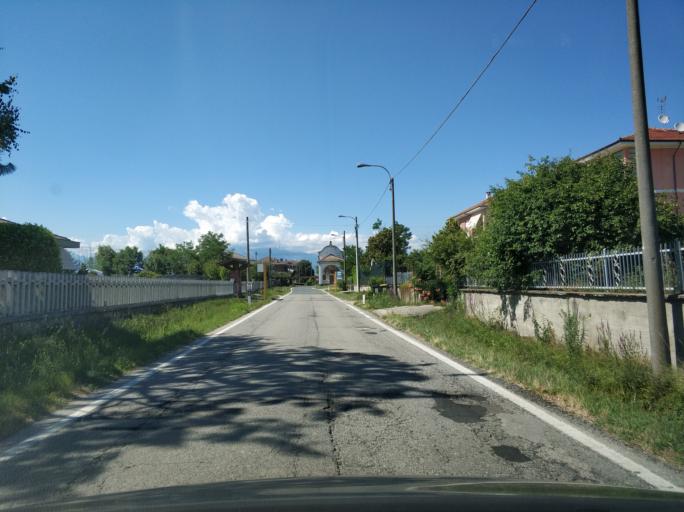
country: IT
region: Piedmont
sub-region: Provincia di Torino
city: San Benigno Canavese
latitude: 45.2347
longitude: 7.7744
